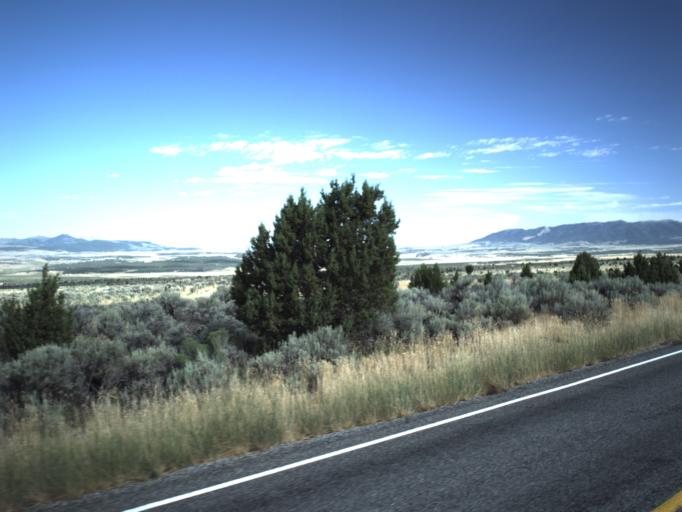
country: US
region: Utah
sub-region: Juab County
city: Mona
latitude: 39.8116
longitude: -112.1430
